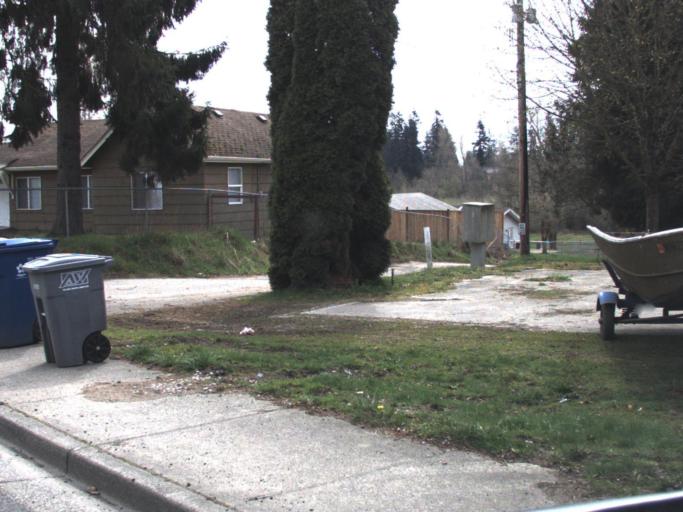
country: US
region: Washington
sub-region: King County
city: Lea Hill
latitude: 47.3646
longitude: -122.1802
